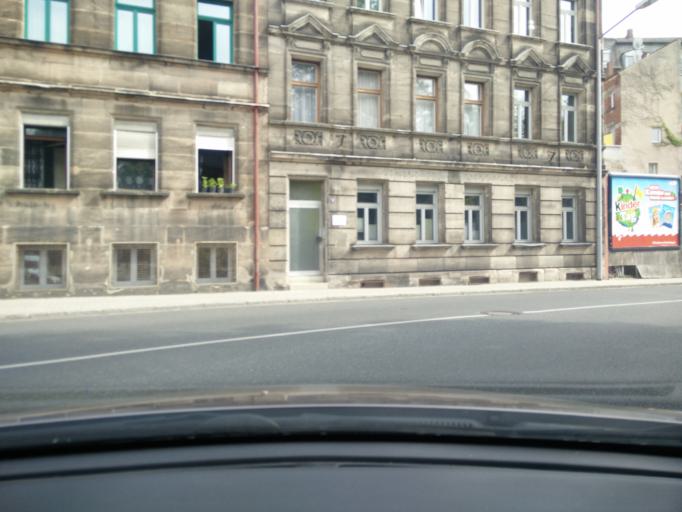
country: DE
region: Bavaria
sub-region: Regierungsbezirk Mittelfranken
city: Furth
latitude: 49.4751
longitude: 10.9817
